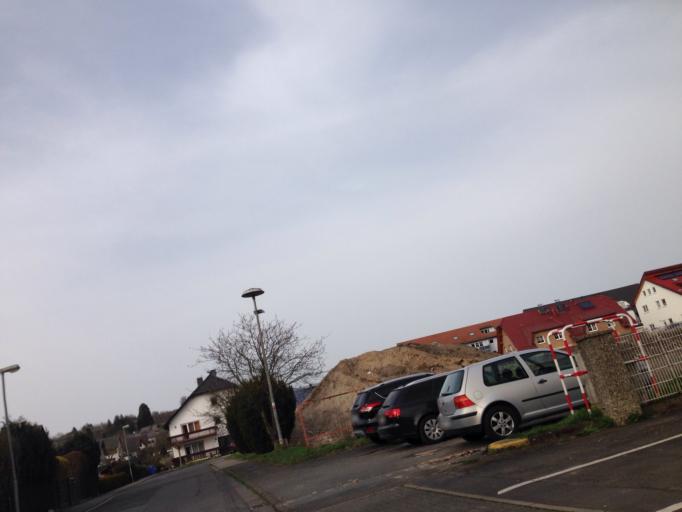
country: DE
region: Hesse
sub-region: Regierungsbezirk Giessen
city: Grossen Buseck
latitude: 50.6063
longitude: 8.7937
